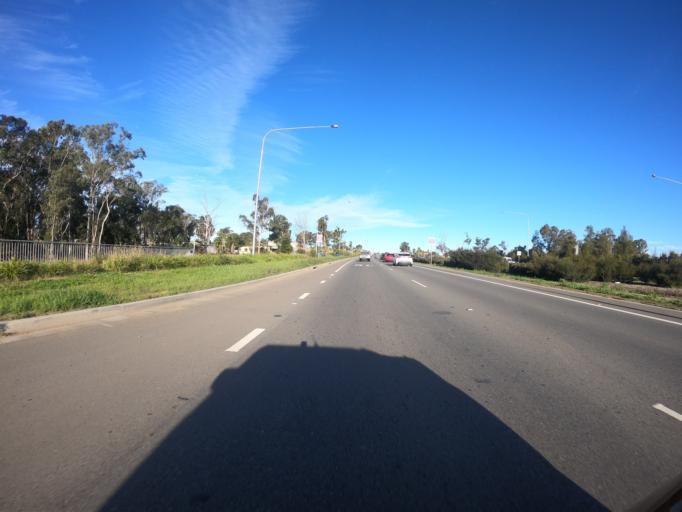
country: AU
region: New South Wales
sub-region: Blacktown
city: Hassall Grove
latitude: -33.7014
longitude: 150.8352
